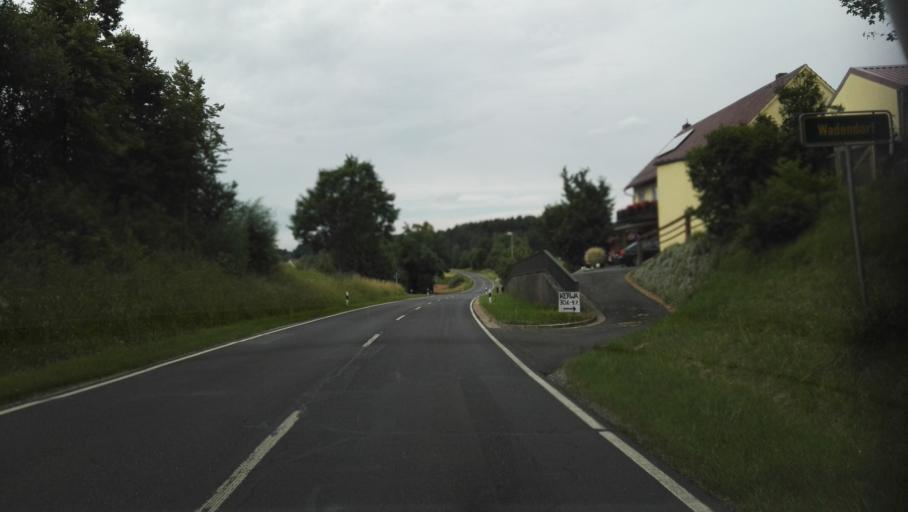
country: DE
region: Bavaria
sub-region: Upper Franconia
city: Plankenfels
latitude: 49.8950
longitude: 11.3336
